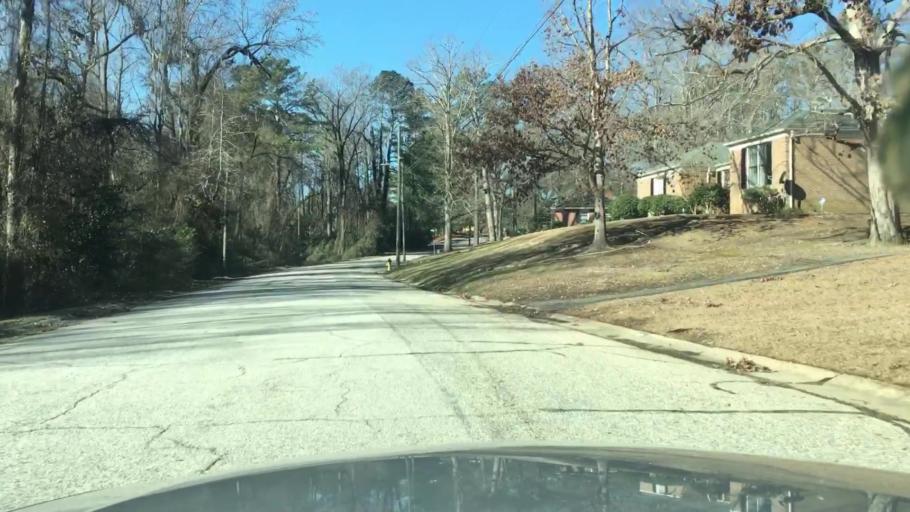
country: US
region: North Carolina
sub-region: Cumberland County
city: Fayetteville
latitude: 35.0766
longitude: -78.9184
